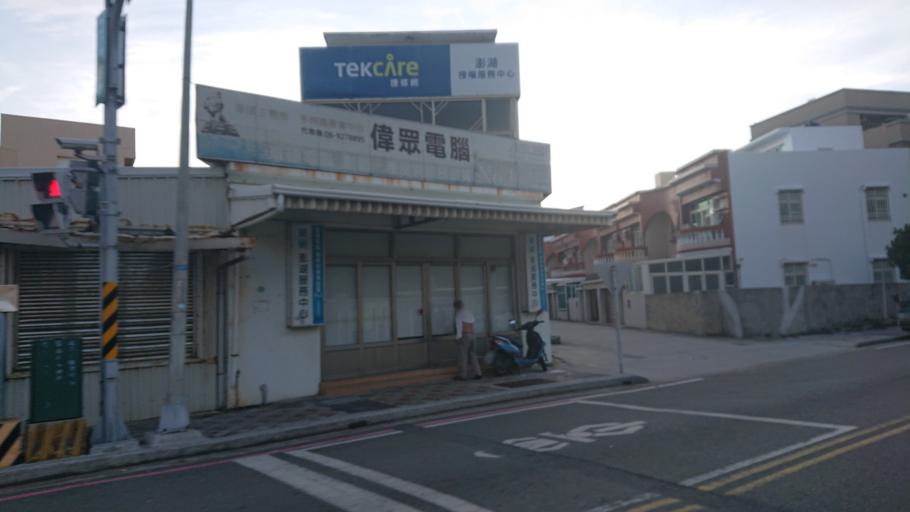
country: TW
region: Taiwan
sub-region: Penghu
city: Ma-kung
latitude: 23.5747
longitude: 119.5809
